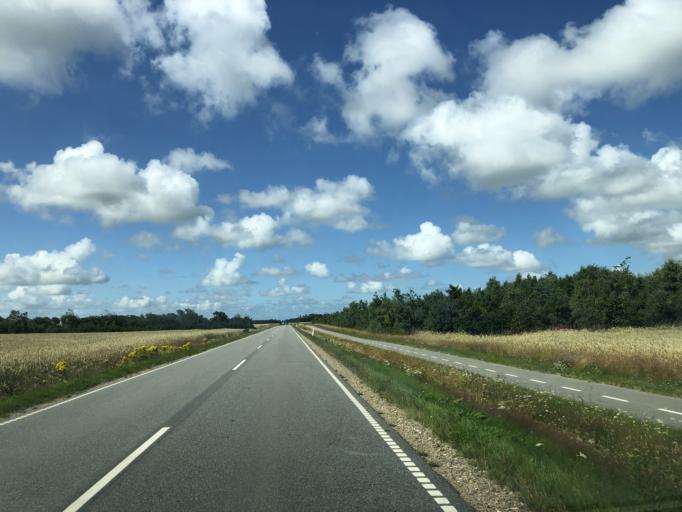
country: DK
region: Central Jutland
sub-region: Holstebro Kommune
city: Ulfborg
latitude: 56.3637
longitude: 8.4074
